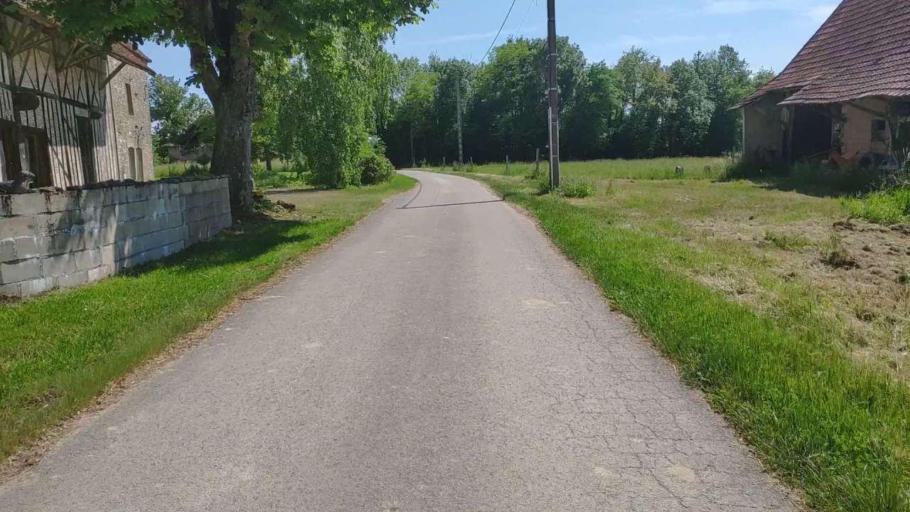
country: FR
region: Franche-Comte
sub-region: Departement du Jura
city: Bletterans
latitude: 46.7966
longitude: 5.4145
